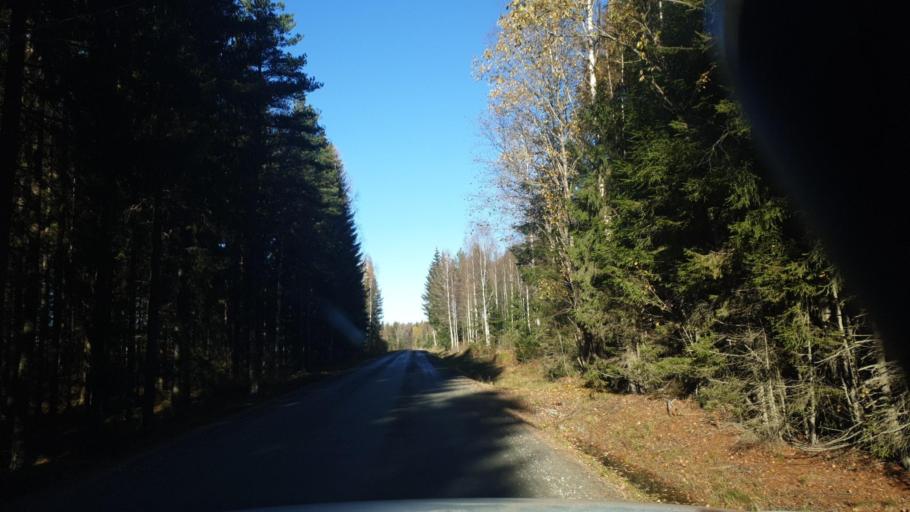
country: SE
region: Vaermland
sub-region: Karlstads Kommun
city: Edsvalla
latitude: 59.4850
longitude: 13.0681
